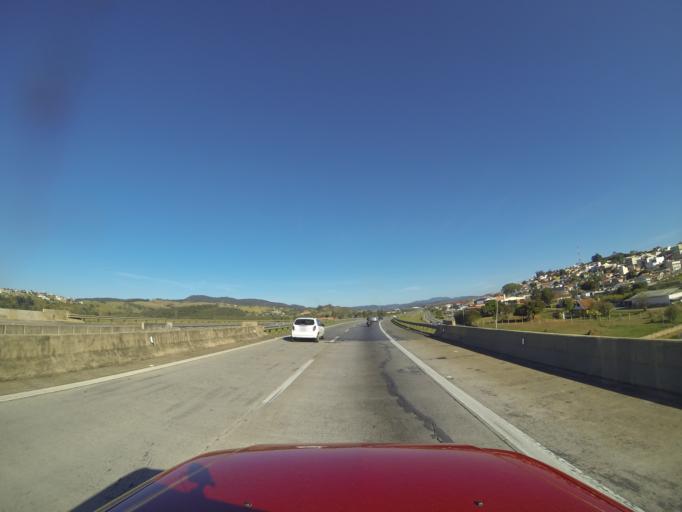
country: BR
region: Sao Paulo
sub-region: Bom Jesus Dos Perdoes
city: Bom Jesus dos Perdoes
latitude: -23.1316
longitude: -46.4621
